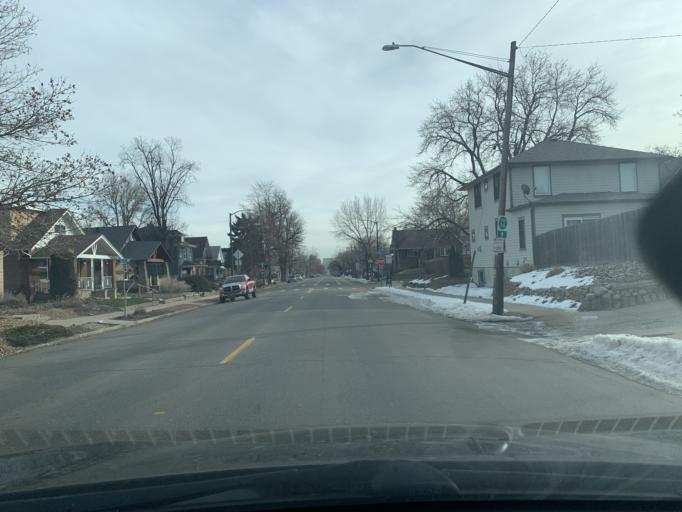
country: US
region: Colorado
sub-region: Jefferson County
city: Edgewater
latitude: 39.7512
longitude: -105.0354
